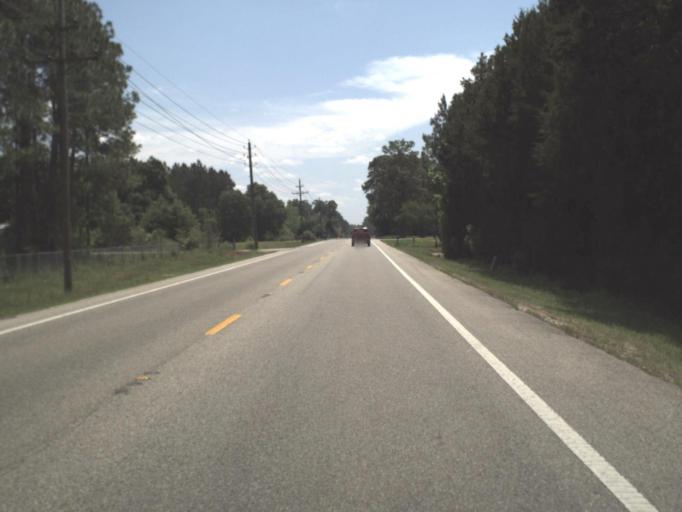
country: US
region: Florida
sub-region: Calhoun County
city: Blountstown
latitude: 30.4991
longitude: -85.1146
